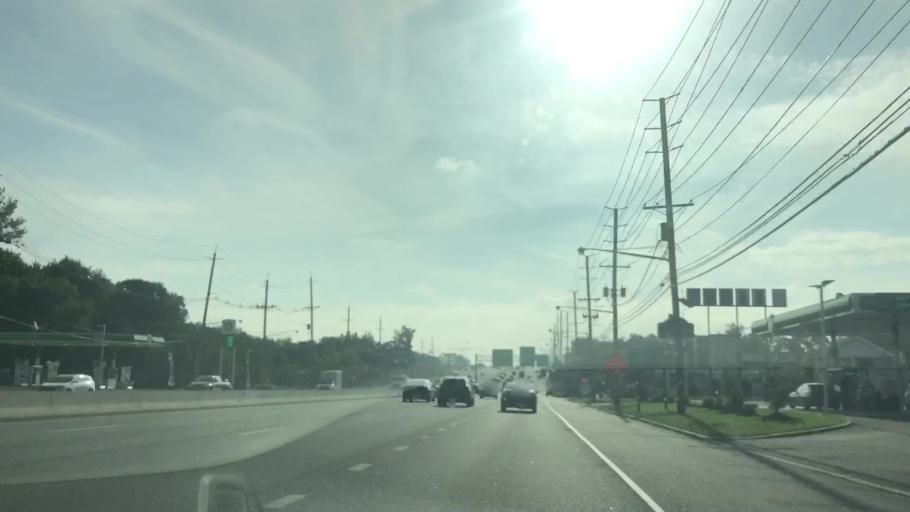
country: US
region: New Jersey
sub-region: Bergen County
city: Lyndhurst
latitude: 40.8283
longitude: -74.1358
